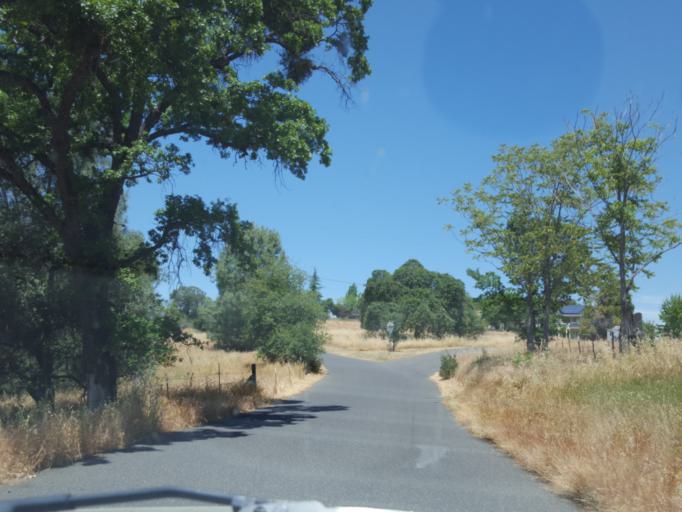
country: US
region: California
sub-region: Calaveras County
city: Angels Camp
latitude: 38.0702
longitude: -120.5485
